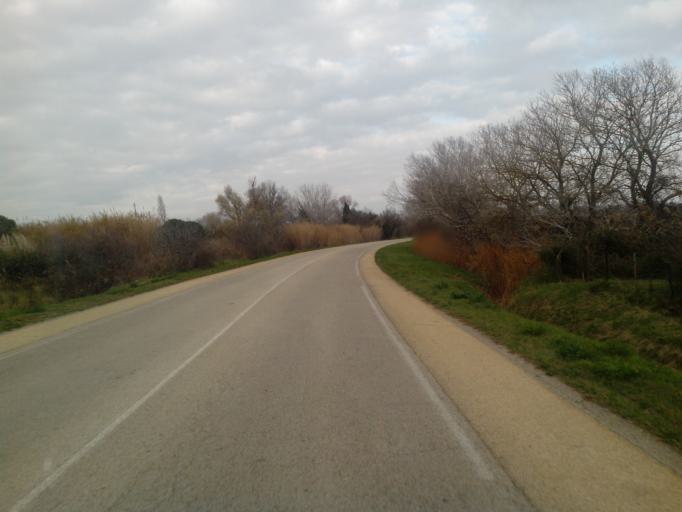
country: FR
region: Provence-Alpes-Cote d'Azur
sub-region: Departement des Bouches-du-Rhone
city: Saintes-Maries-de-la-Mer
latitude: 43.5487
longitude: 4.4016
